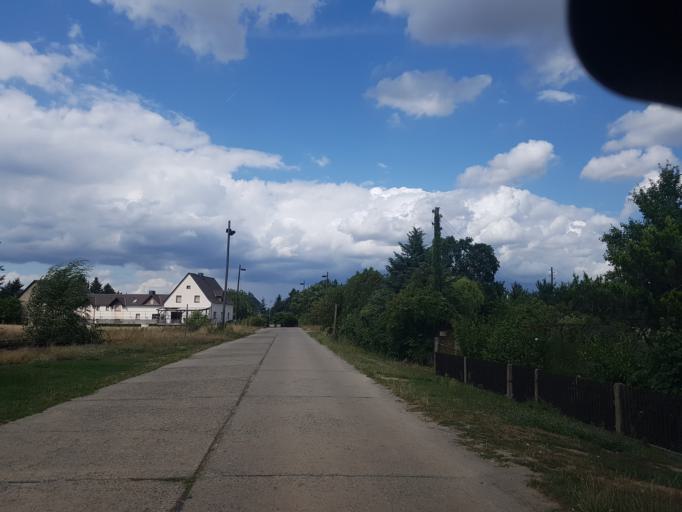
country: DE
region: Brandenburg
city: Herzberg
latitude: 51.6833
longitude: 13.2367
